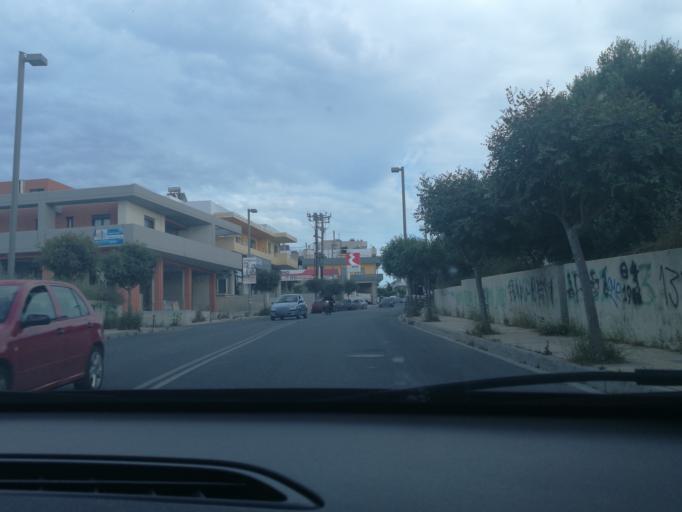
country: GR
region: Crete
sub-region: Nomos Irakleiou
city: Irakleion
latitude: 35.3154
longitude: 25.1337
